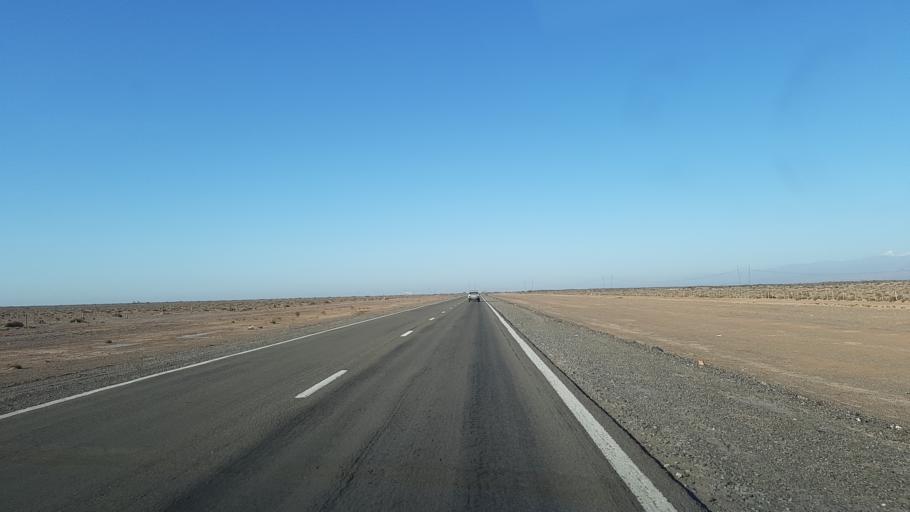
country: AR
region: San Juan
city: Villa Media Agua
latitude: -32.3292
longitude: -68.5392
